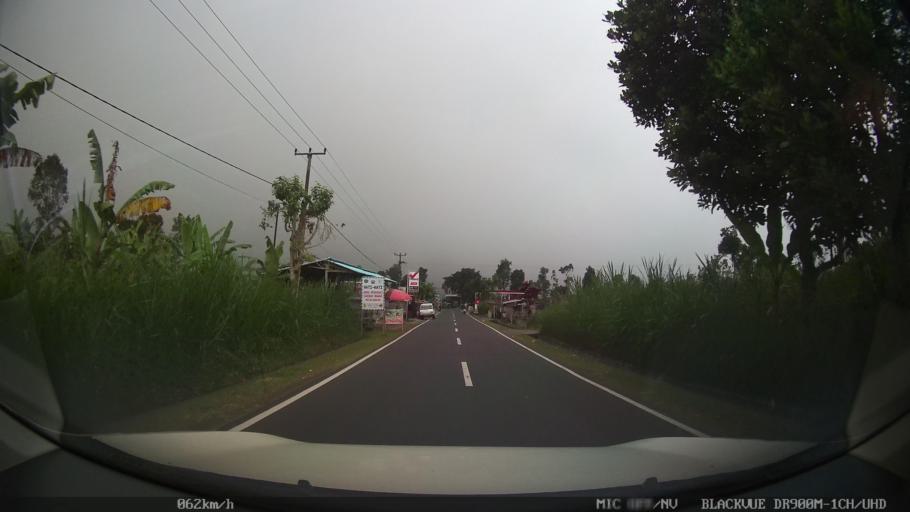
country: ID
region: Bali
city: Banjar Kedisan
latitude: -8.2857
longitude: 115.3199
